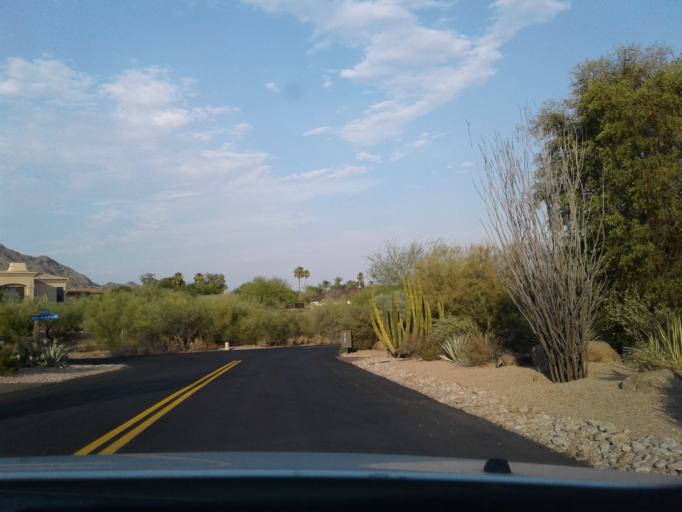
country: US
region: Arizona
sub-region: Maricopa County
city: Paradise Valley
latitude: 33.5349
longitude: -111.9859
